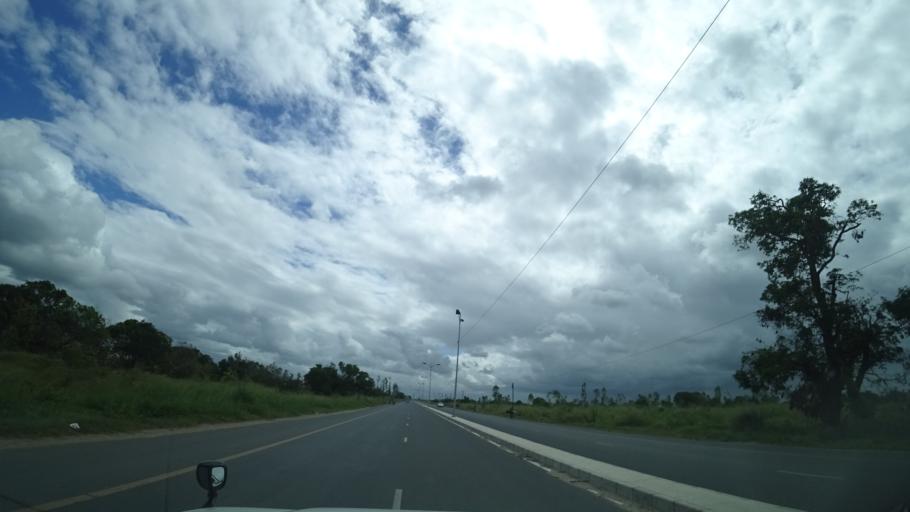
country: MZ
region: Sofala
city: Dondo
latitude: -19.5912
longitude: 34.7376
